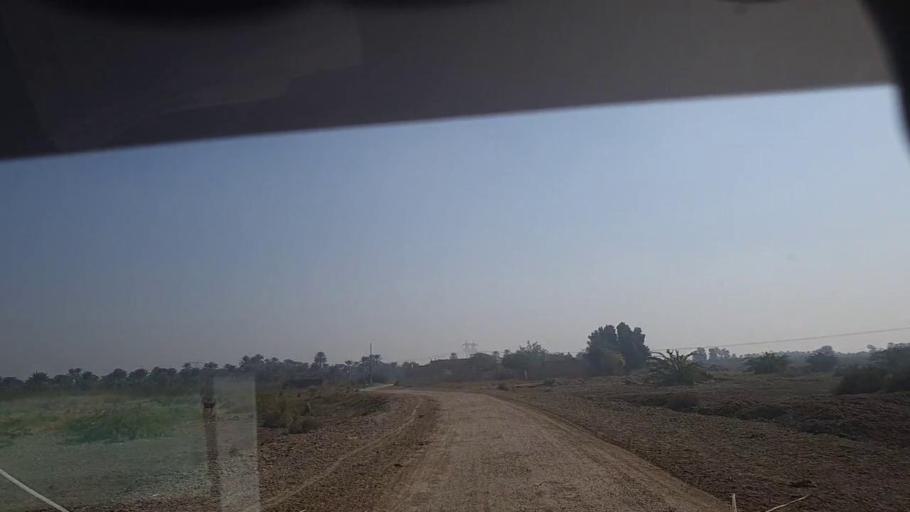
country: PK
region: Sindh
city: Khairpur
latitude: 27.4597
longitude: 68.7390
